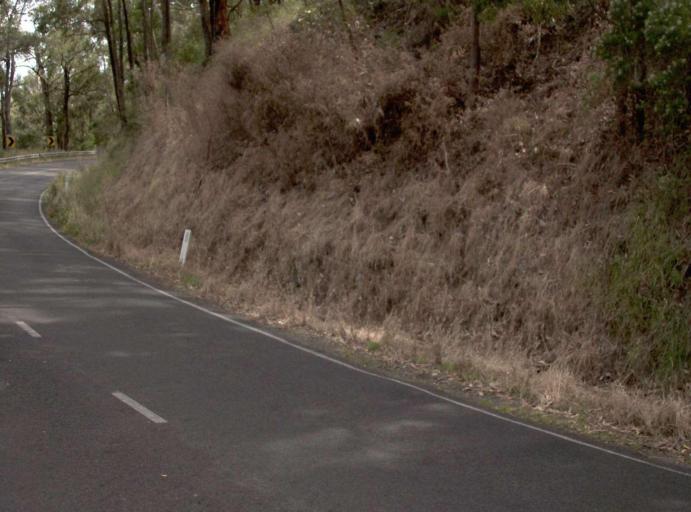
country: AU
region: Victoria
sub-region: Latrobe
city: Moe
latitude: -38.2330
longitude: 146.1661
